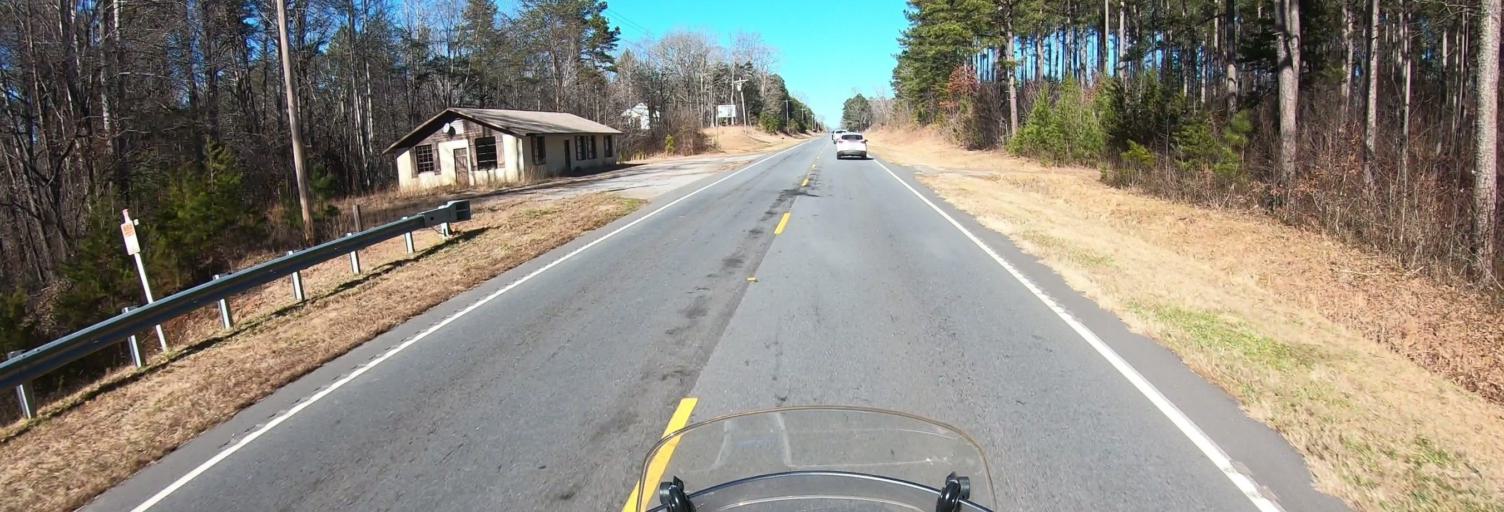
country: US
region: South Carolina
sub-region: Oconee County
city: Westminster
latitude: 34.6348
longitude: -83.1352
